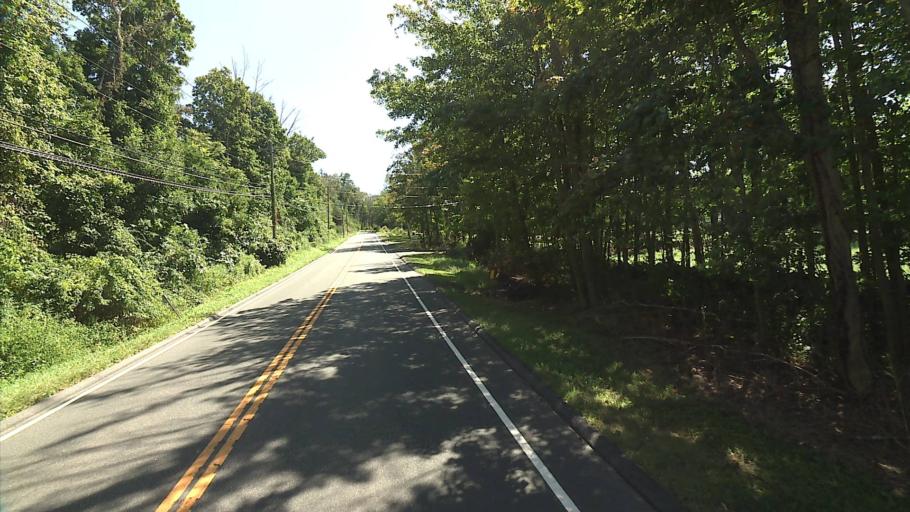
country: US
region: Connecticut
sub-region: New Haven County
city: Oxford
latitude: 41.4184
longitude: -73.1495
